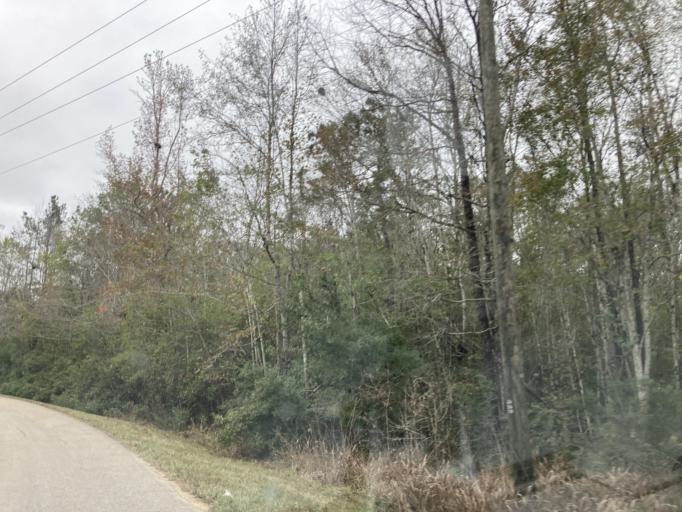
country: US
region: Mississippi
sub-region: Lamar County
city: West Hattiesburg
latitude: 31.2537
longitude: -89.4945
